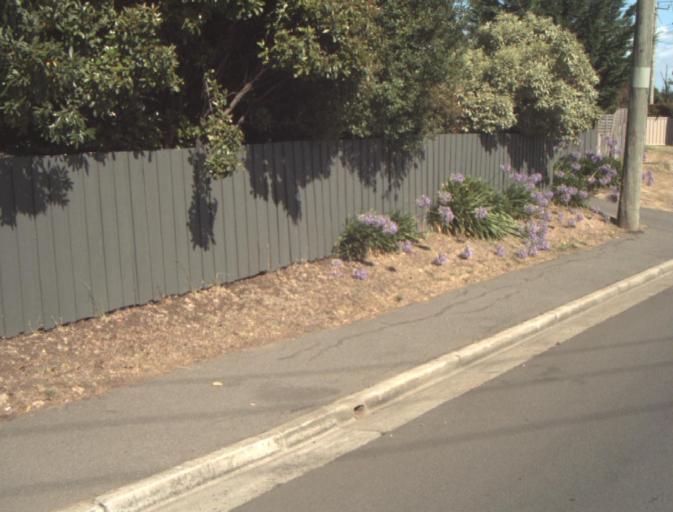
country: AU
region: Tasmania
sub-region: Launceston
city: Newstead
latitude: -41.4361
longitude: 147.1757
